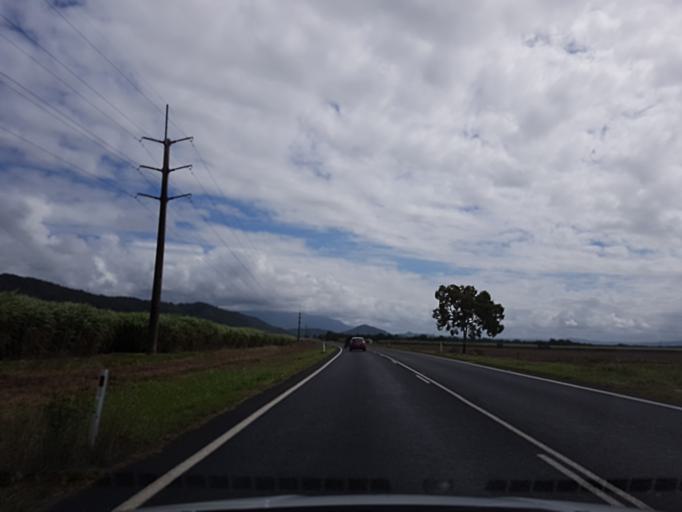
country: AU
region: Queensland
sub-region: Cairns
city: Port Douglas
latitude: -16.5074
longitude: 145.4405
